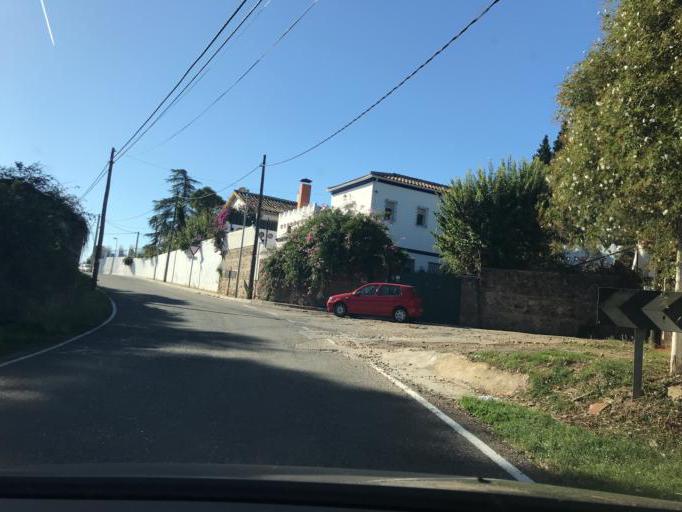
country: ES
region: Andalusia
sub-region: Province of Cordoba
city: Cordoba
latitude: 37.9279
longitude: -4.8064
